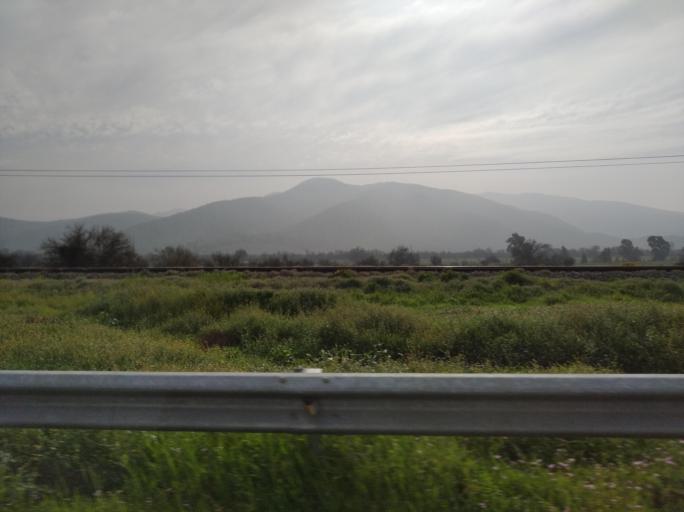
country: CL
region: Santiago Metropolitan
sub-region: Provincia de Chacabuco
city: Lampa
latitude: -33.1522
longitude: -70.9051
